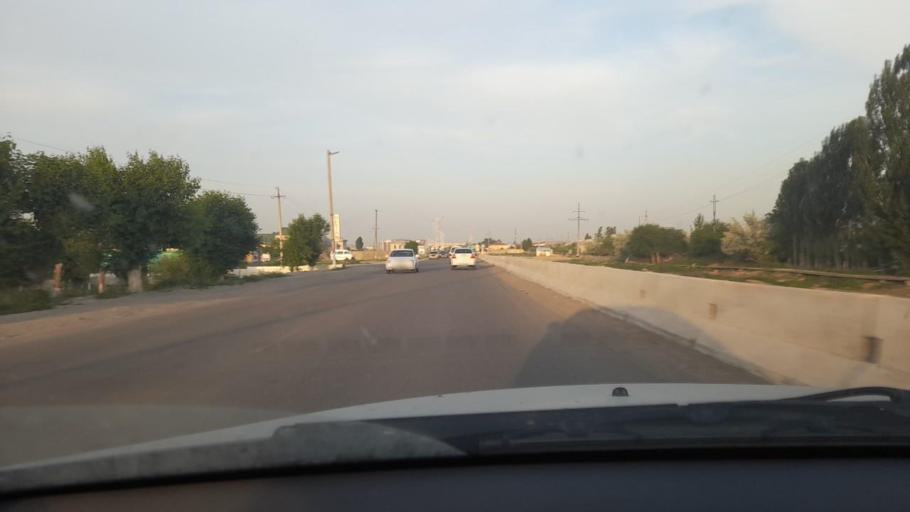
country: UZ
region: Sirdaryo
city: Guliston
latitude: 40.5073
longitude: 68.7467
